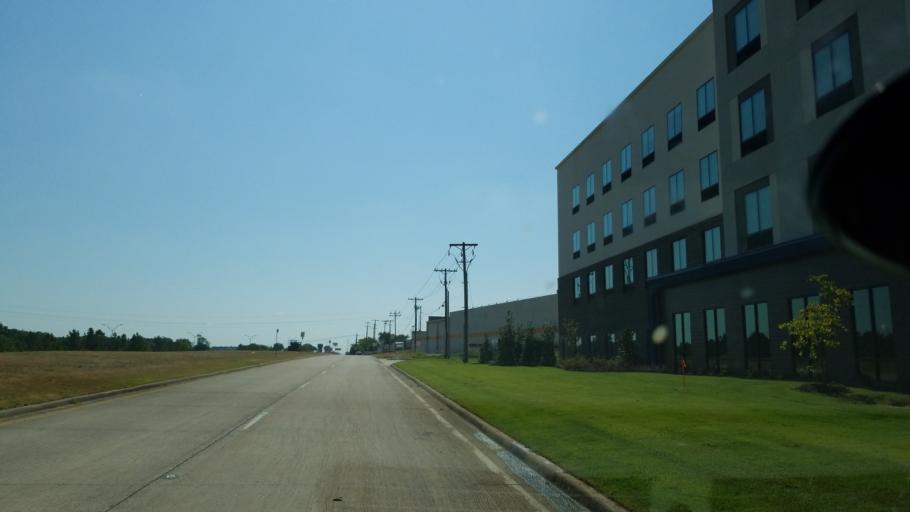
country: US
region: Texas
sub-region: Dallas County
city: Duncanville
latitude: 32.6636
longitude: -96.9040
